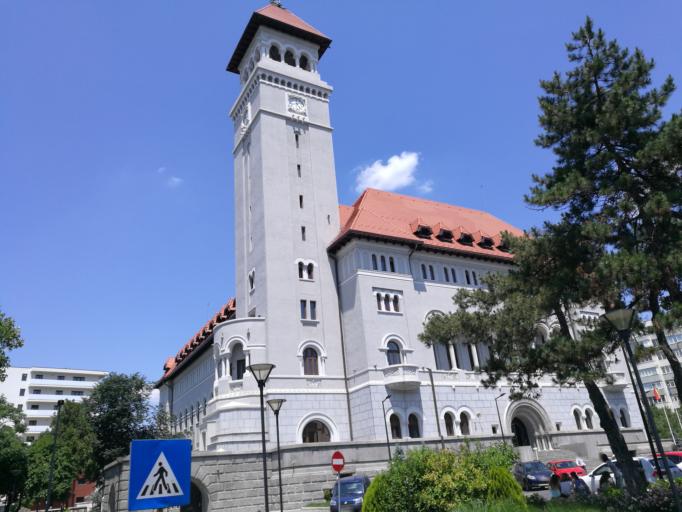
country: RO
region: Bucuresti
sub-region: Municipiul Bucuresti
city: Bucuresti
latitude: 44.4535
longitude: 26.0739
